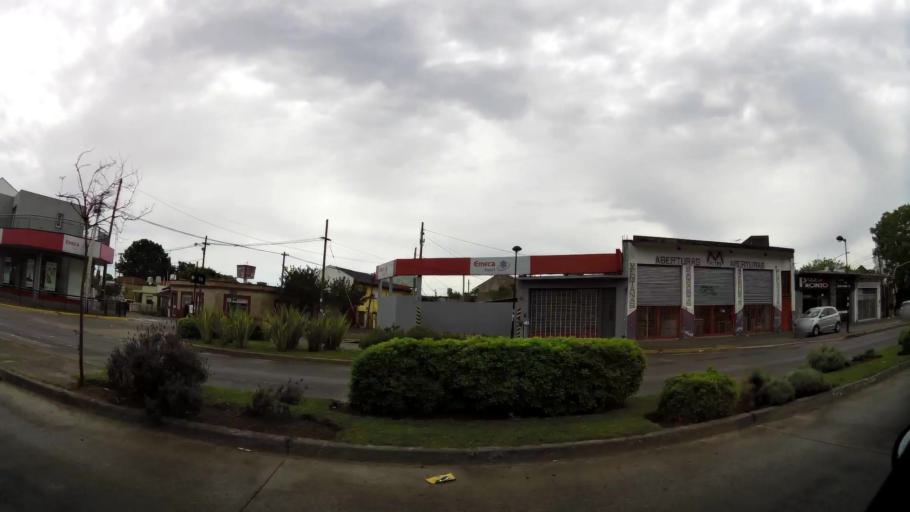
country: AR
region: Buenos Aires
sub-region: Partido de Quilmes
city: Quilmes
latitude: -34.7542
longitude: -58.2117
